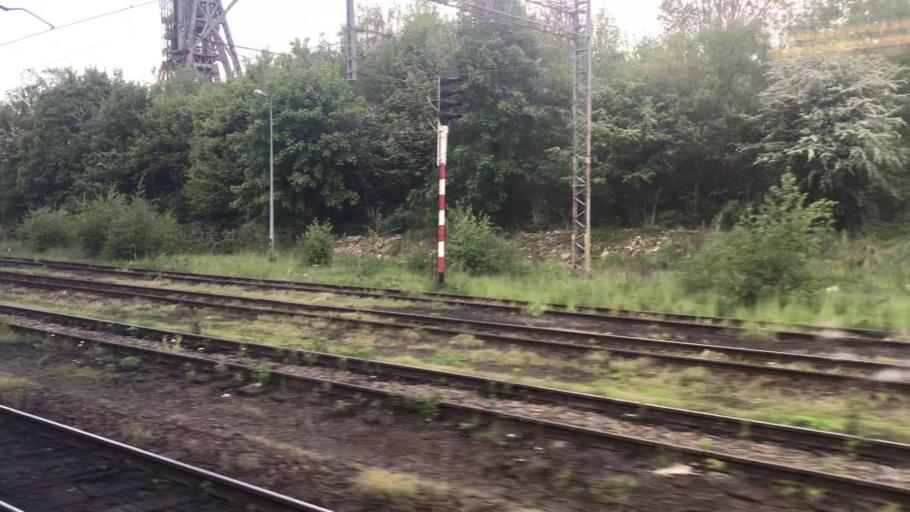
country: PL
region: Lower Silesian Voivodeship
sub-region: Powiat walbrzyski
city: Walbrzych
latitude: 50.7626
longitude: 16.2654
